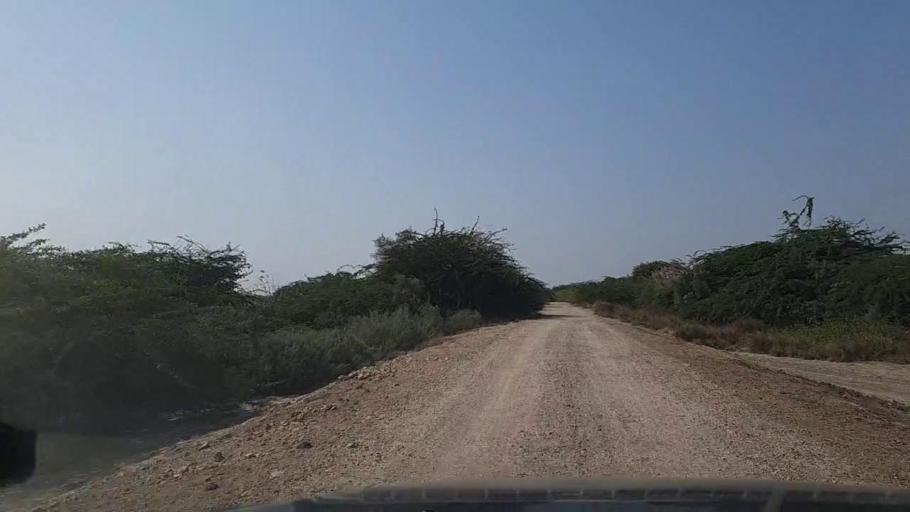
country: PK
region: Sindh
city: Mirpur Sakro
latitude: 24.4308
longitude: 67.7194
